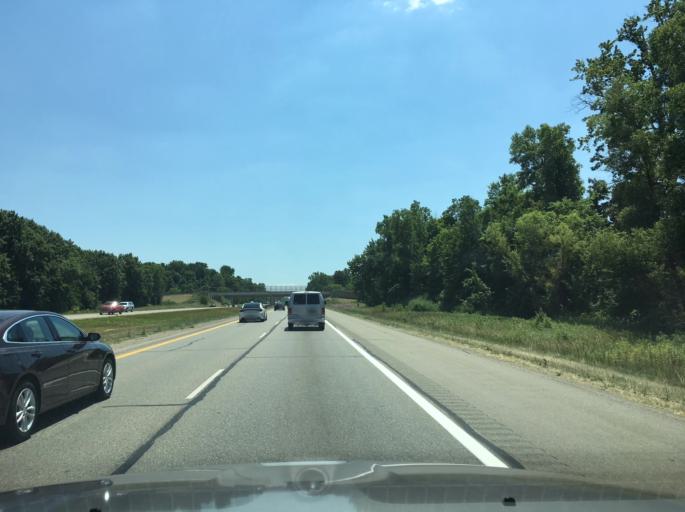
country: US
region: Michigan
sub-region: Macomb County
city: Shelby
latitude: 42.6583
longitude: -83.0145
